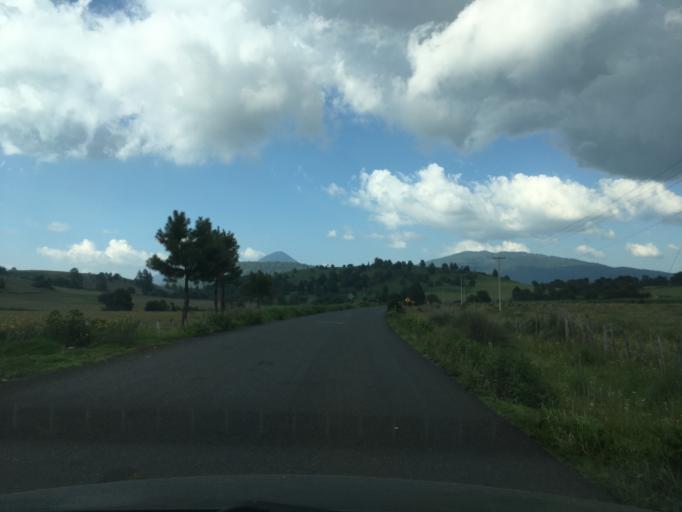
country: MX
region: Michoacan
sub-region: Nahuatzen
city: Sevina
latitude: 19.6104
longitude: -101.9375
